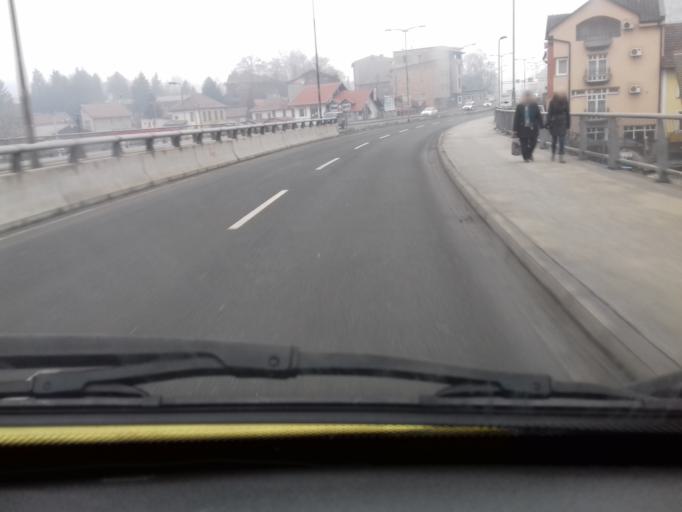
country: BA
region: Federation of Bosnia and Herzegovina
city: Zenica
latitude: 44.1978
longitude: 17.9053
